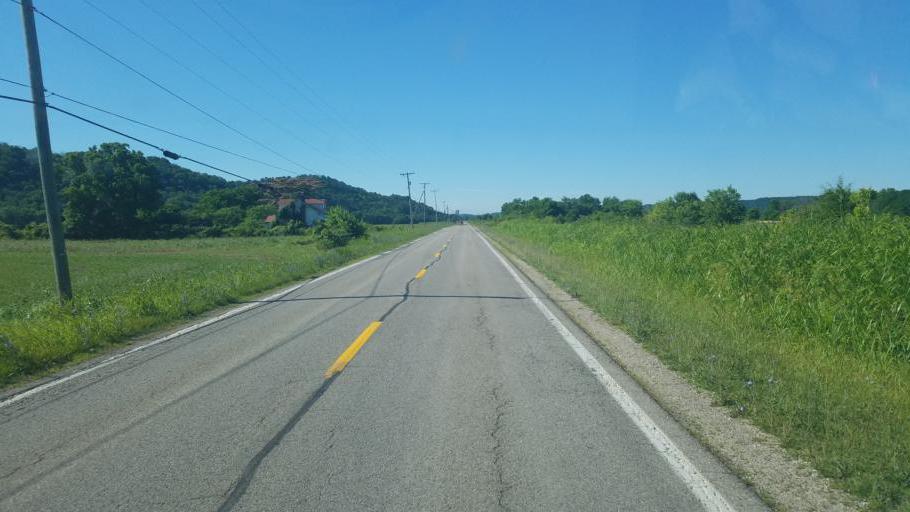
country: US
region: Ohio
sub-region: Gallia County
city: Gallipolis
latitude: 38.7181
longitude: -82.1786
